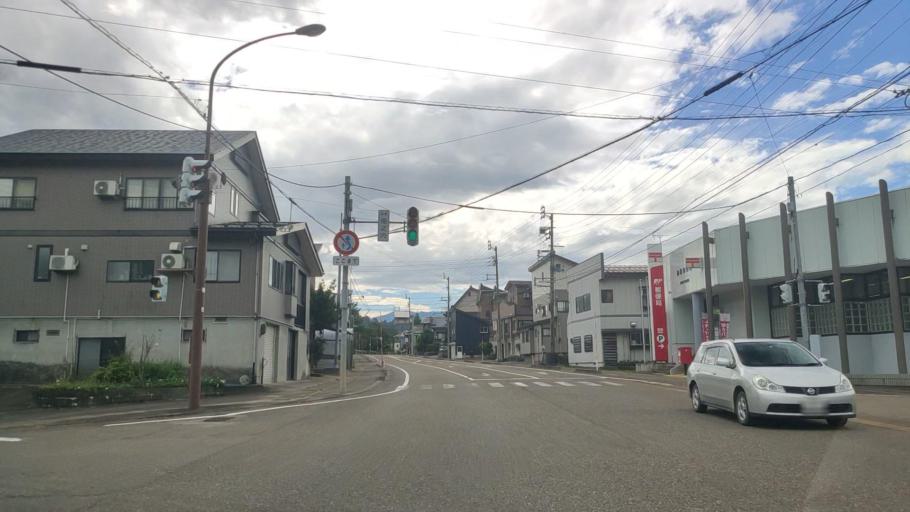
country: JP
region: Niigata
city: Arai
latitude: 36.9874
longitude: 138.2716
